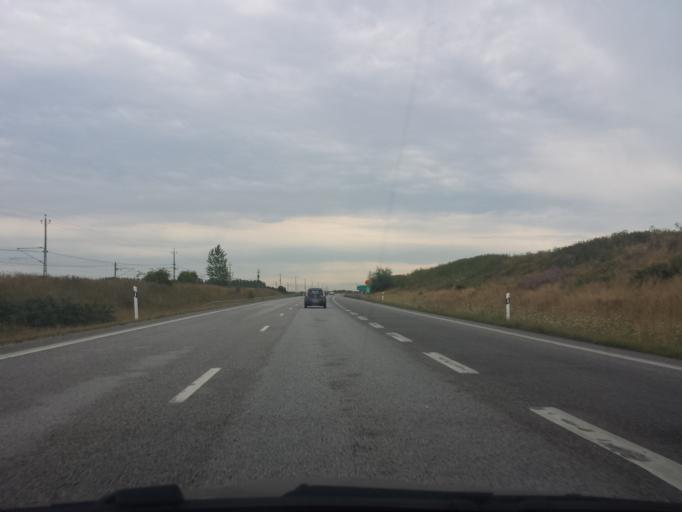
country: SE
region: Skane
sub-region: Malmo
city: Bunkeflostrand
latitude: 55.5585
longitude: 12.9392
